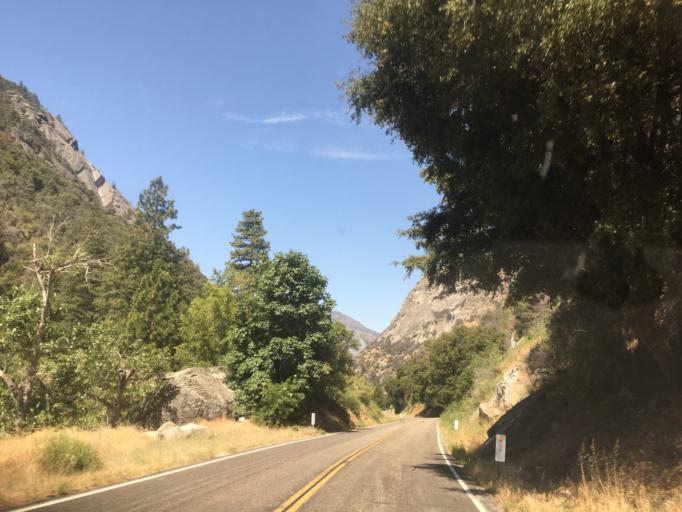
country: US
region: California
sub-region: Tulare County
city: Three Rivers
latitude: 36.8087
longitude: -118.7694
